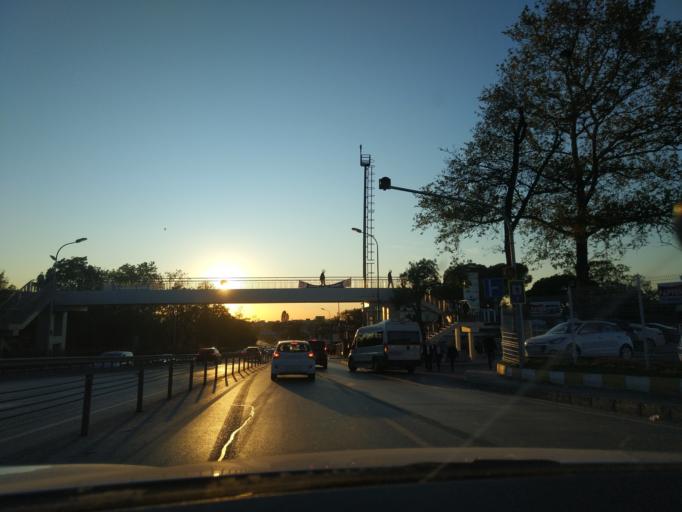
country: TR
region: Istanbul
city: UEskuedar
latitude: 41.0239
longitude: 29.0542
